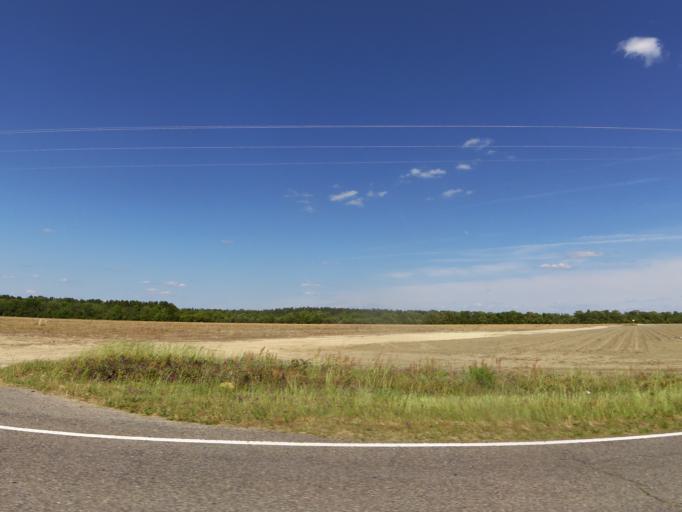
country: US
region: South Carolina
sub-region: Barnwell County
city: Williston
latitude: 33.4401
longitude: -81.4871
